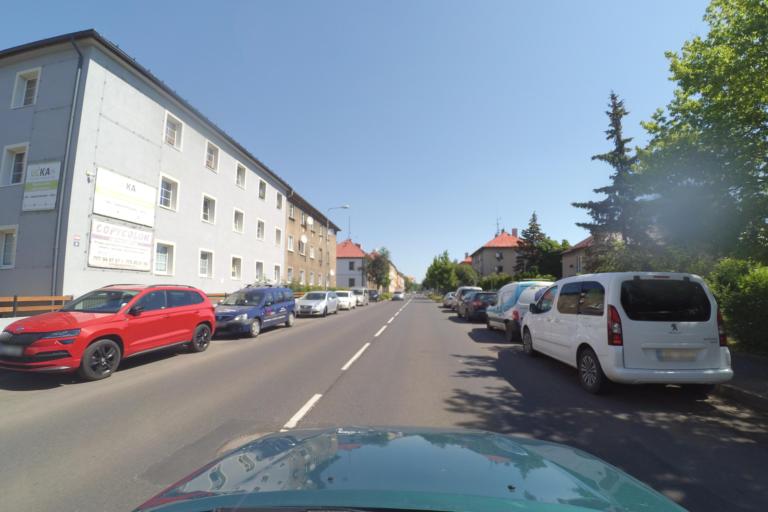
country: CZ
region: Ustecky
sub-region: Okres Chomutov
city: Chomutov
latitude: 50.4607
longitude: 13.3987
